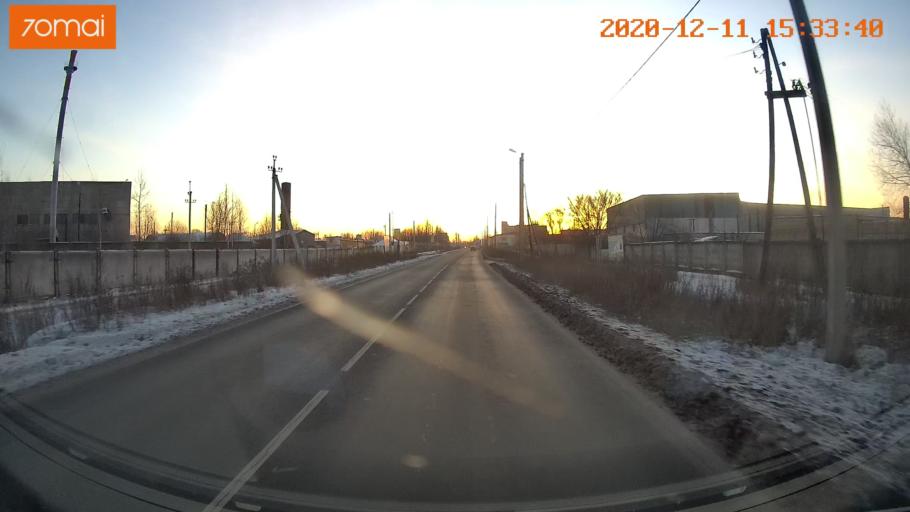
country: RU
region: Ivanovo
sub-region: Gorod Ivanovo
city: Ivanovo
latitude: 57.0504
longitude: 40.9456
